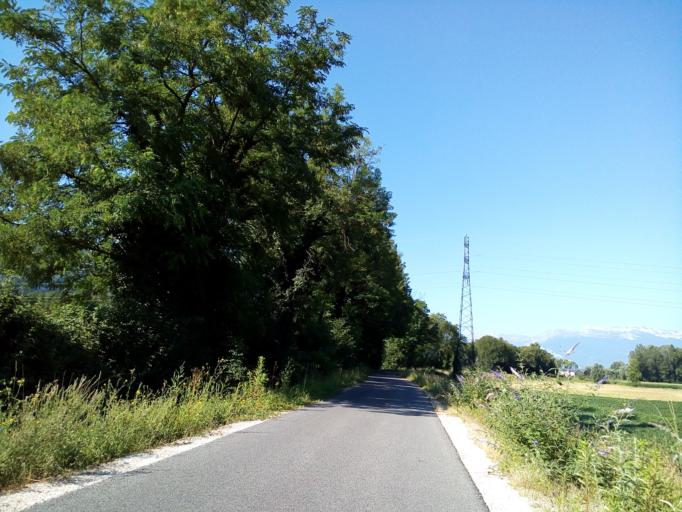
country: FR
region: Rhone-Alpes
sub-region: Departement de l'Isere
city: Domene
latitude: 45.2063
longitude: 5.8235
